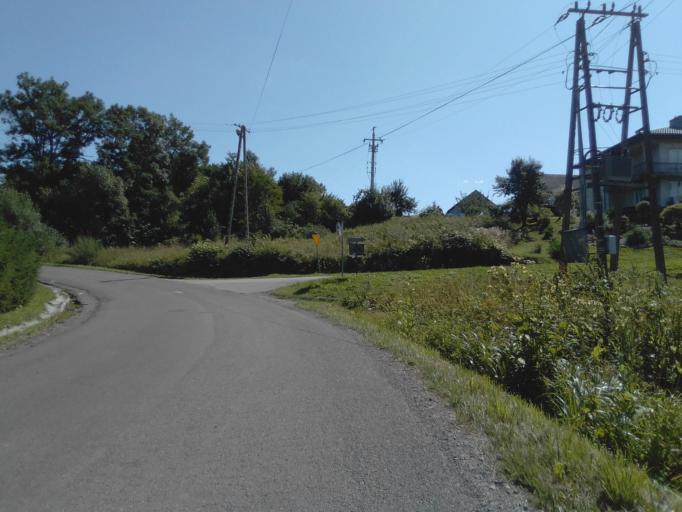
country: PL
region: Subcarpathian Voivodeship
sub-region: Powiat krosnienski
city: Chorkowka
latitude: 49.6380
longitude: 21.6102
